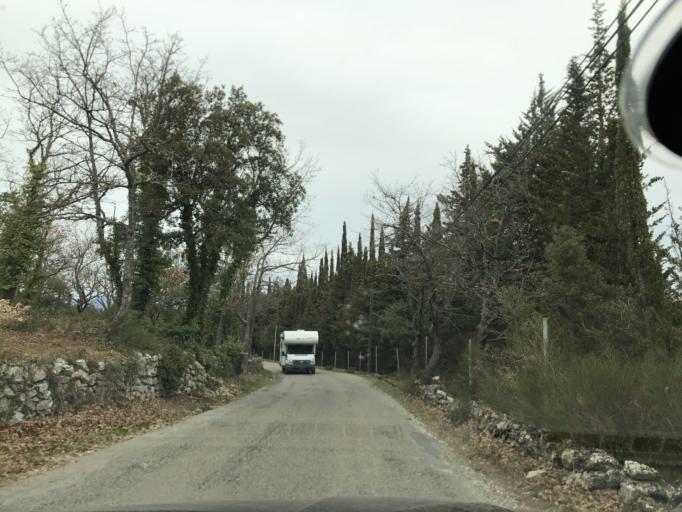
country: FR
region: Provence-Alpes-Cote d'Azur
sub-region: Departement du Vaucluse
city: Bonnieux
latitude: 43.8094
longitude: 5.3154
